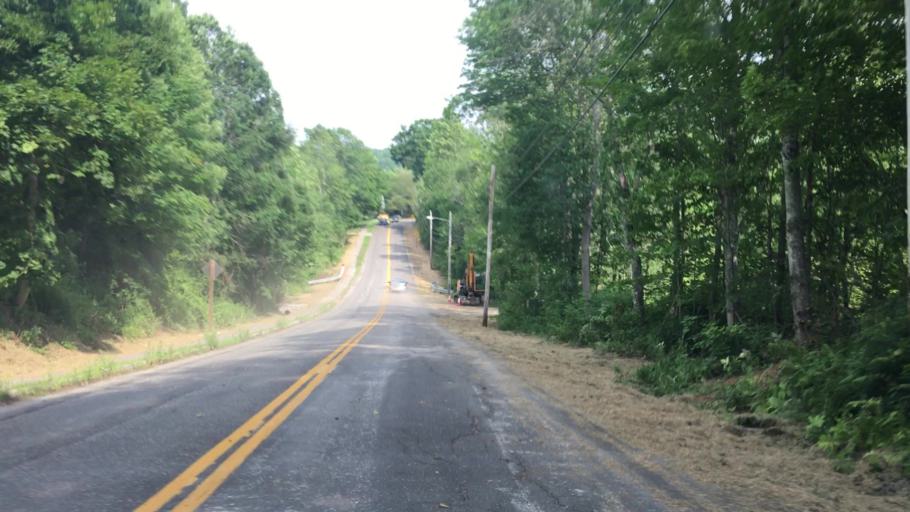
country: US
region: Maine
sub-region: Lincoln County
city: Waldoboro
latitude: 44.0956
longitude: -69.3835
